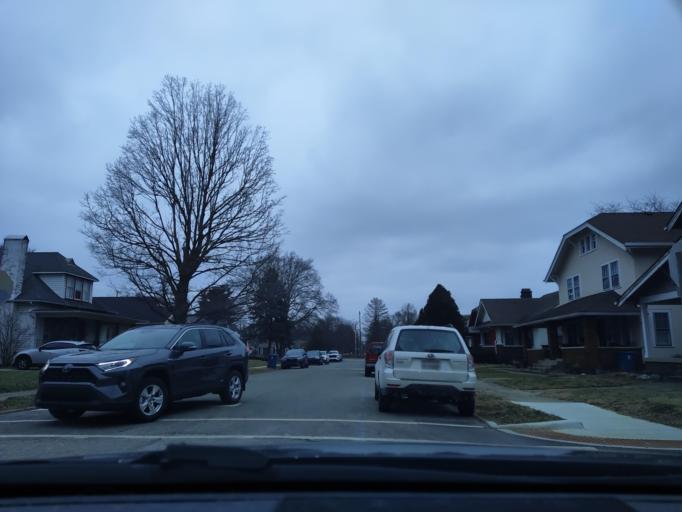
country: US
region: Indiana
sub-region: Marion County
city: Broad Ripple
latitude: 39.8680
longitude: -86.1475
